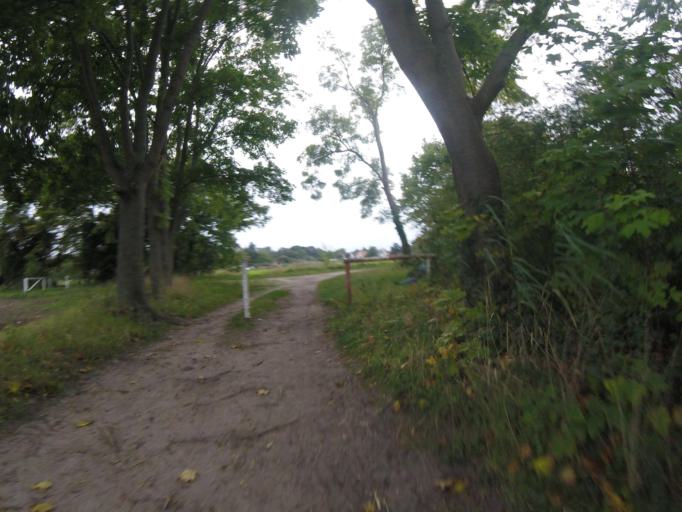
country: DE
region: Brandenburg
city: Mittenwalde
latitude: 52.2663
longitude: 13.5441
